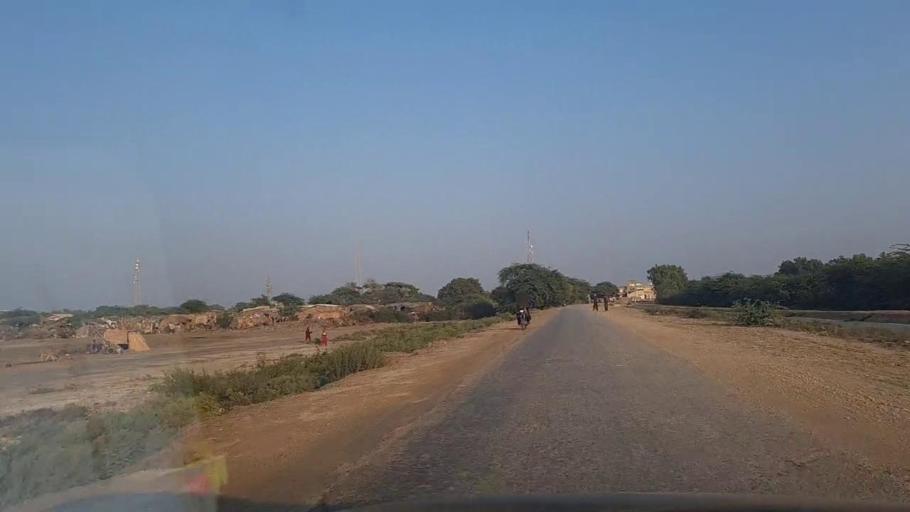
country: PK
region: Sindh
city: Keti Bandar
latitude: 24.3010
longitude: 67.5997
